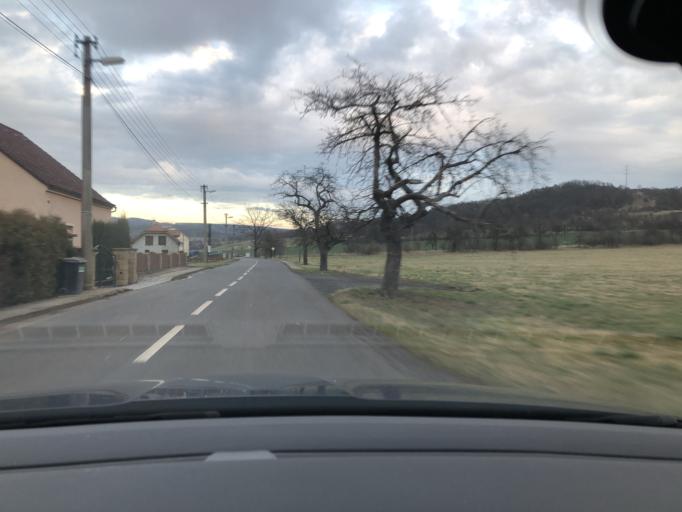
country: CZ
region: Ustecky
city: Rehlovice
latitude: 50.6064
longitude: 13.9347
